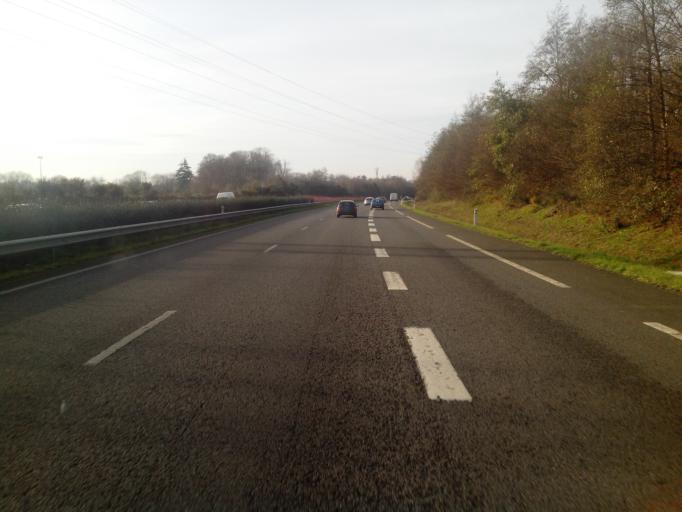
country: FR
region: Brittany
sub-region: Departement d'Ille-et-Vilaine
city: Cesson-Sevigne
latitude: 48.1402
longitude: -1.6328
